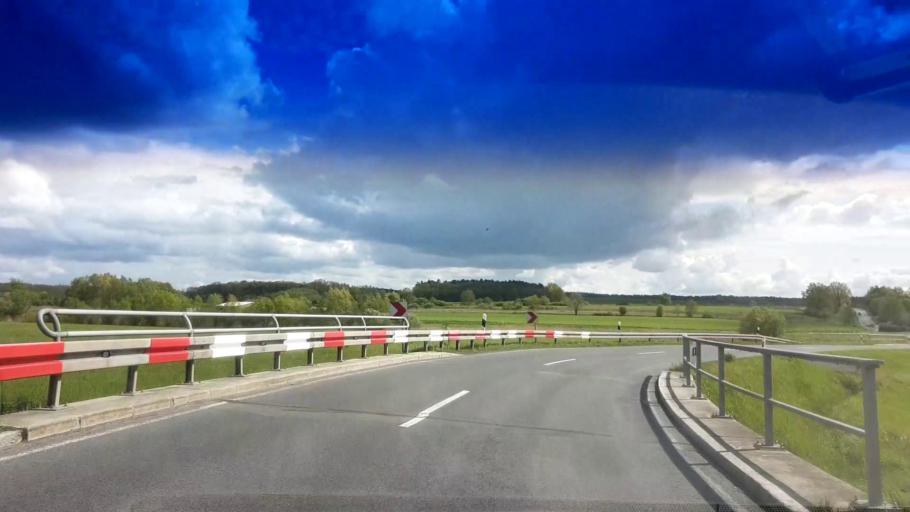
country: DE
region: Bavaria
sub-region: Upper Franconia
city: Frensdorf
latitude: 49.8218
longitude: 10.8424
